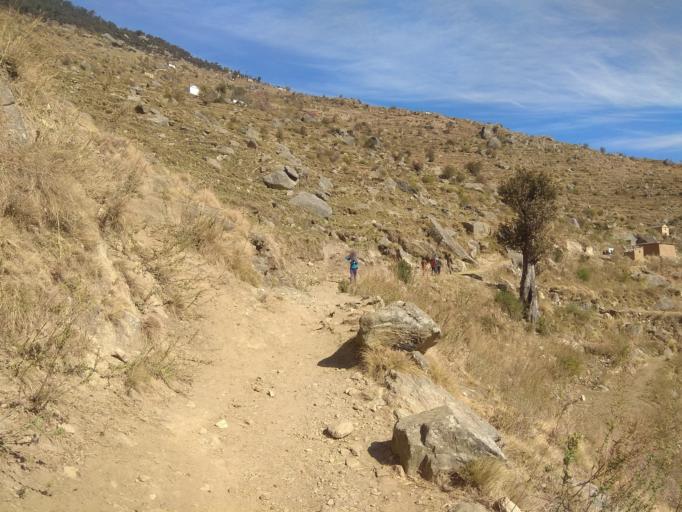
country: NP
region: Mid Western
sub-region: Bheri Zone
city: Dailekh
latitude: 29.2955
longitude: 81.7159
